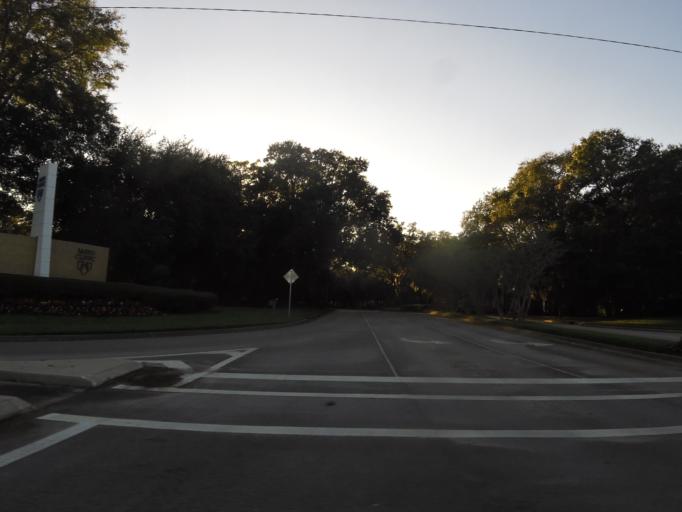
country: US
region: Florida
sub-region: Duval County
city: Jacksonville Beach
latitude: 30.2624
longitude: -81.4375
